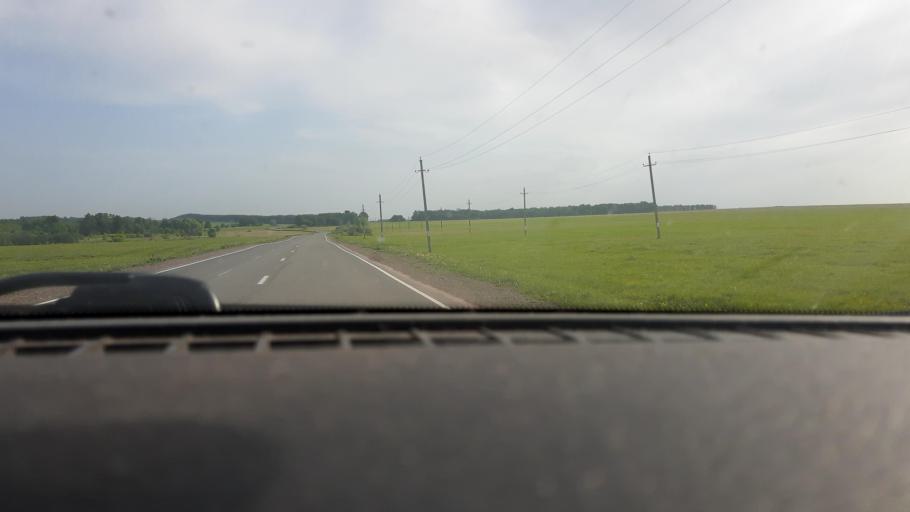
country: RU
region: Bashkortostan
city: Ulukulevo
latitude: 54.5968
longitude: 56.4265
